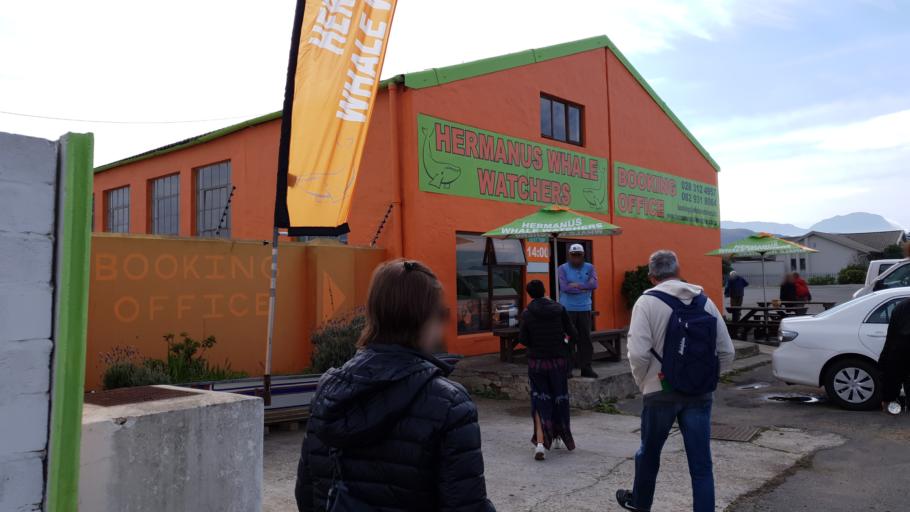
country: ZA
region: Western Cape
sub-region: Overberg District Municipality
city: Hermanus
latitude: -34.4331
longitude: 19.2234
